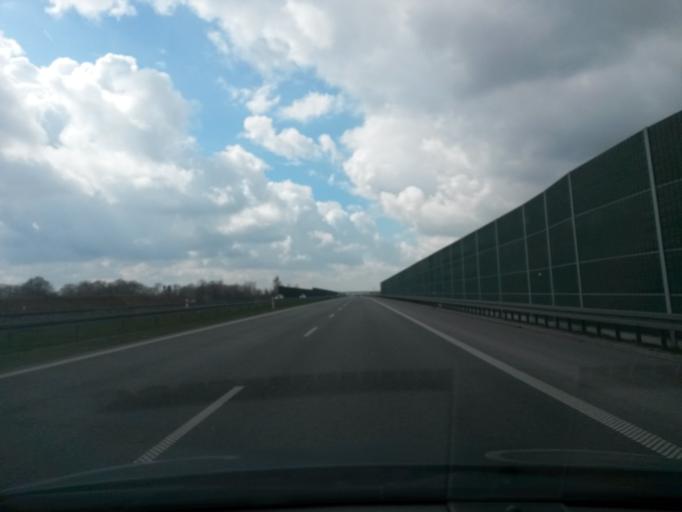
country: PL
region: Masovian Voivodeship
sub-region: Powiat warszawski zachodni
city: Bieniewice
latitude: 52.1405
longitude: 20.5869
